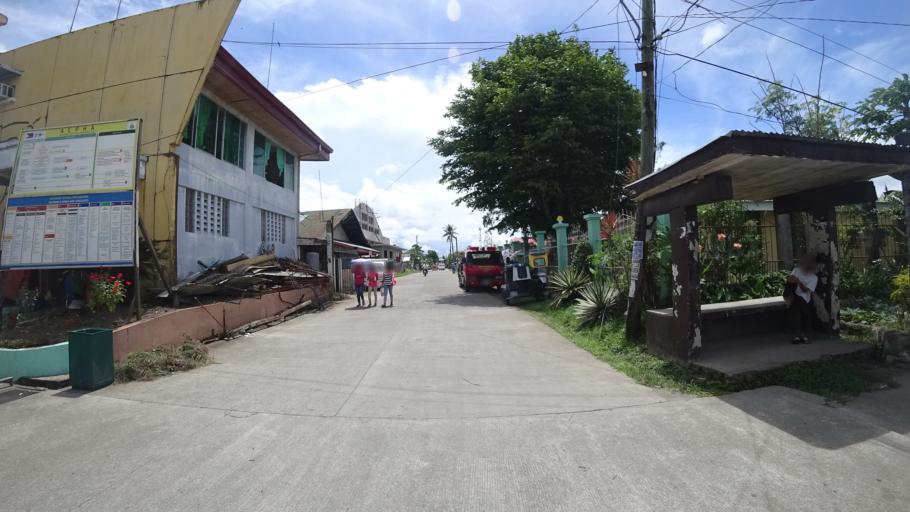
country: PH
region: Eastern Visayas
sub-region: Province of Leyte
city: Alangalang
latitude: 11.2077
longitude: 124.8466
